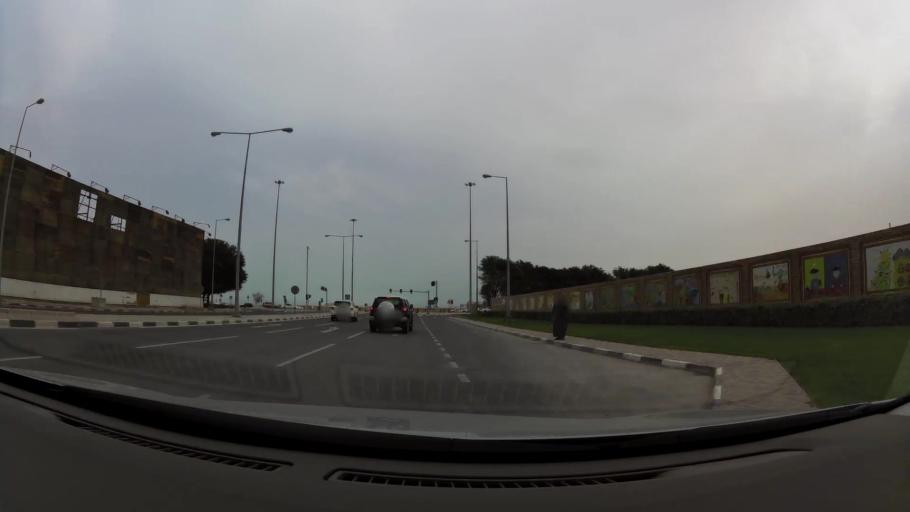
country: QA
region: Baladiyat ad Dawhah
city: Doha
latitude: 25.3120
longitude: 51.5193
